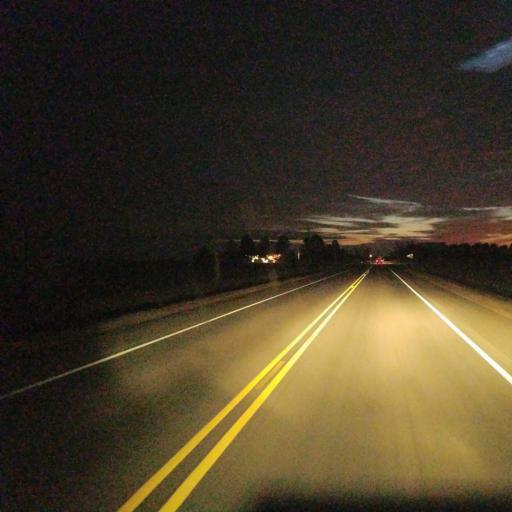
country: US
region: Illinois
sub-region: Fulton County
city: Farmington
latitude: 40.6981
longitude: -89.9251
